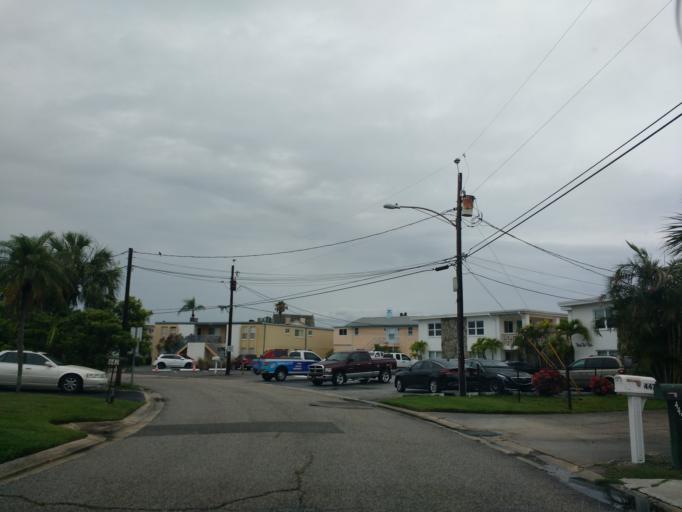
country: US
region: Florida
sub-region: Pinellas County
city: Madeira Beach
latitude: 27.7877
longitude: -82.7804
